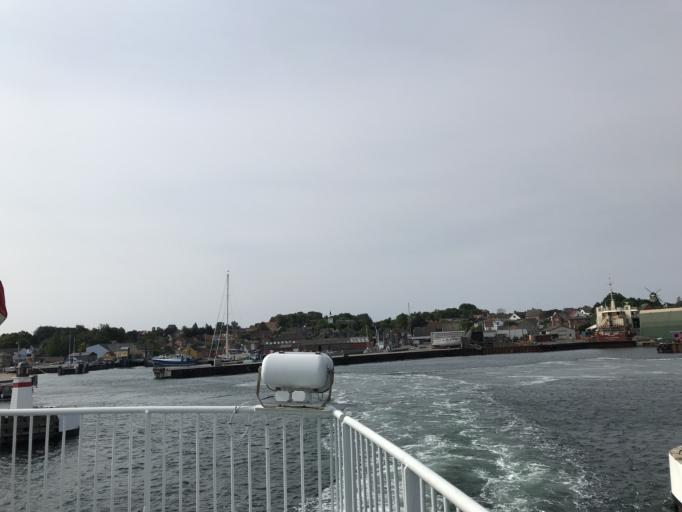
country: DK
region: South Denmark
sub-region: Faaborg-Midtfyn Kommune
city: Faaborg
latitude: 54.9439
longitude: 10.2589
